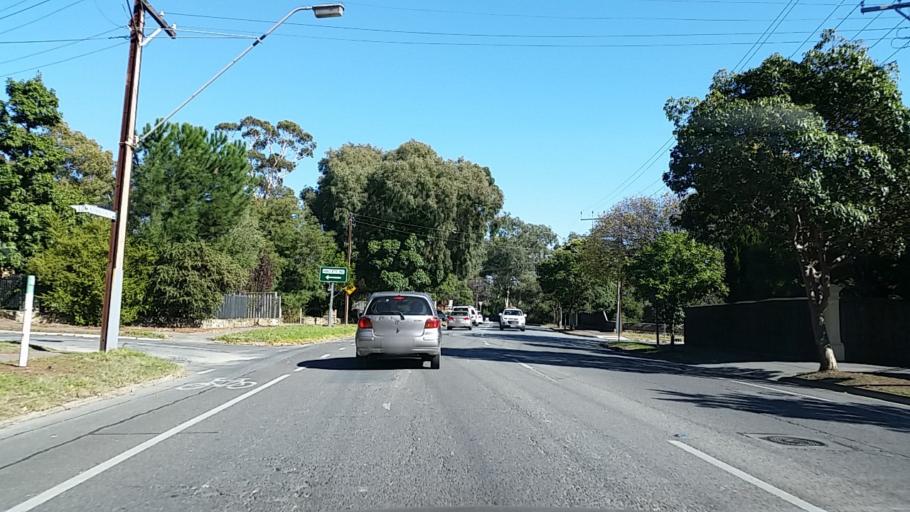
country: AU
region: South Australia
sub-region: Burnside
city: Wattle Park
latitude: -34.9250
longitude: 138.6694
